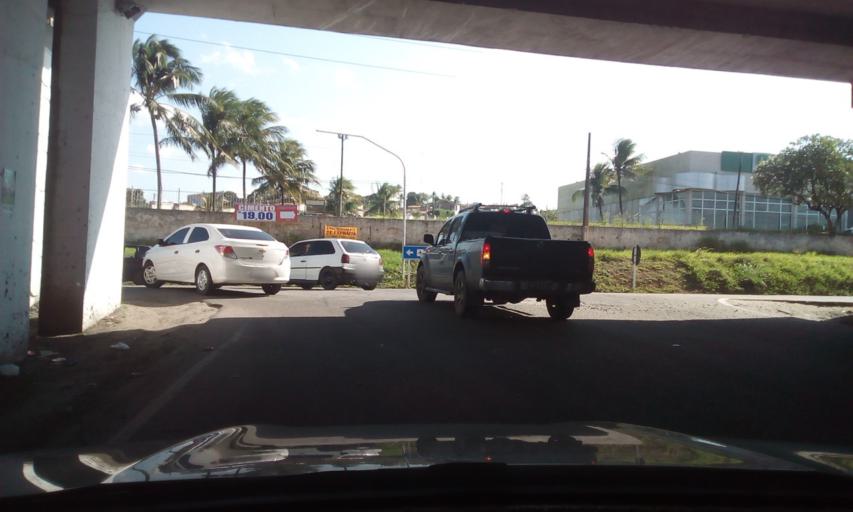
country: BR
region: Paraiba
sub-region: Bayeux
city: Bayeux
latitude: -7.1312
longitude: -34.9328
